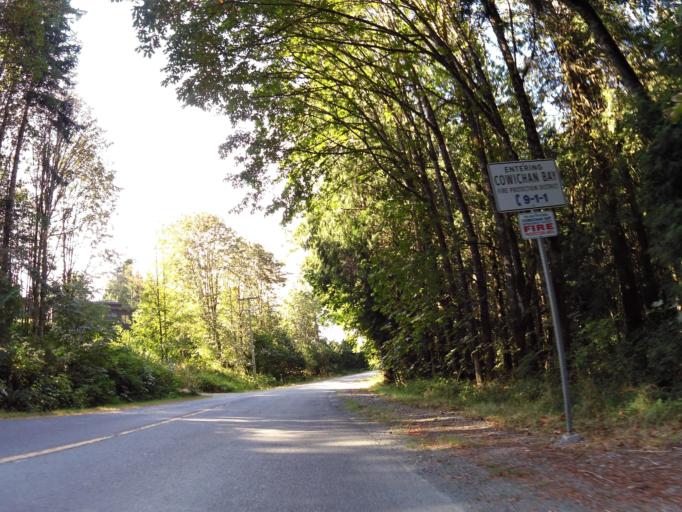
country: CA
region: British Columbia
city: North Saanich
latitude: 48.6939
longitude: -123.5658
